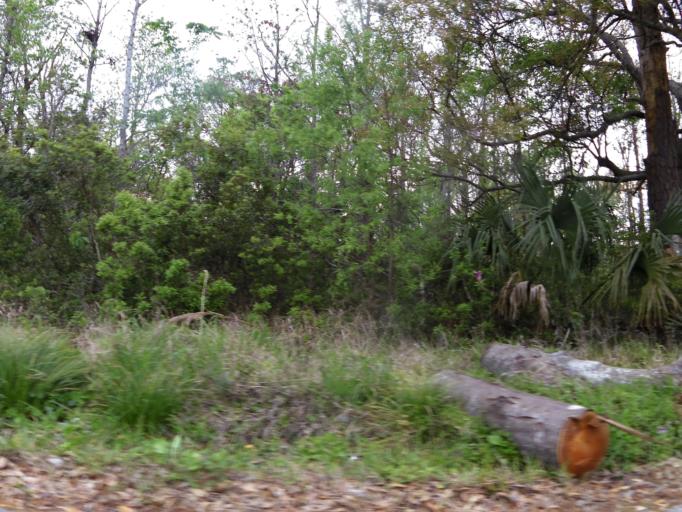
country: US
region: Florida
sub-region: Duval County
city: Jacksonville
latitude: 30.3663
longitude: -81.6329
